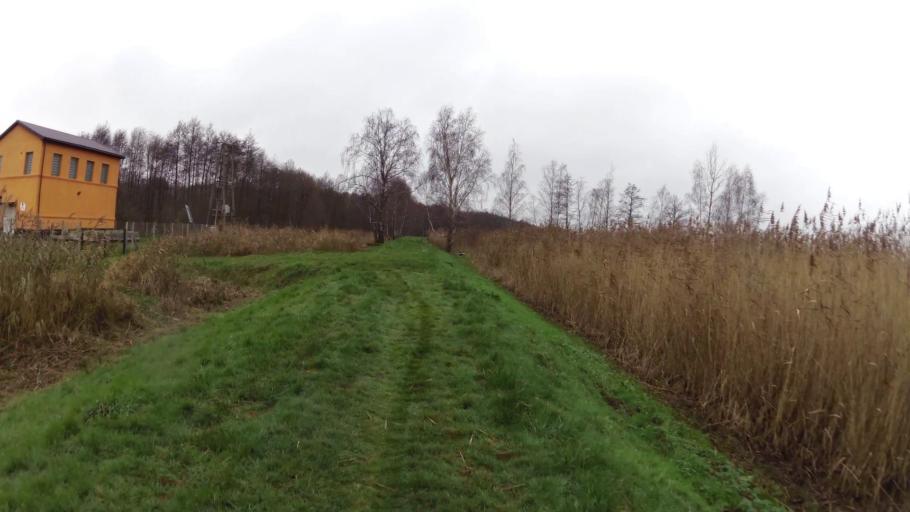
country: PL
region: West Pomeranian Voivodeship
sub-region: Powiat koszalinski
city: Mielno
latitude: 54.2512
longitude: 16.1284
